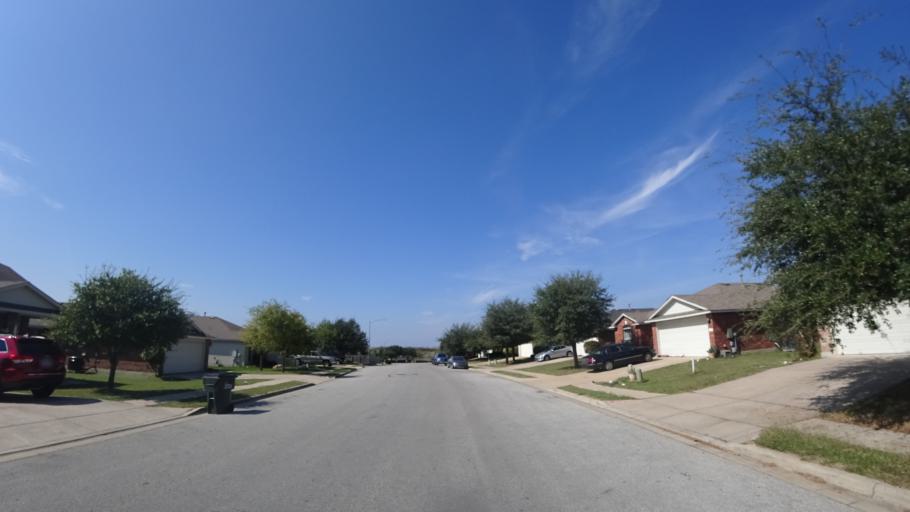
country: US
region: Texas
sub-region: Travis County
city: Pflugerville
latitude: 30.4269
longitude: -97.6395
